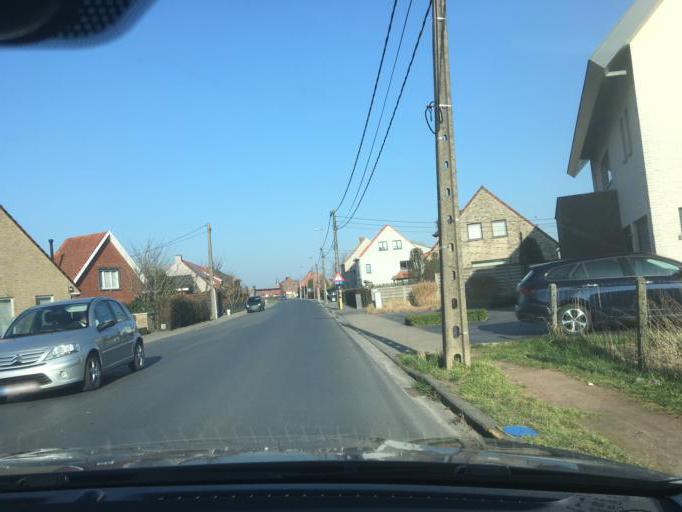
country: BE
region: Flanders
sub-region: Provincie West-Vlaanderen
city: Ledegem
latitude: 50.8624
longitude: 3.1369
